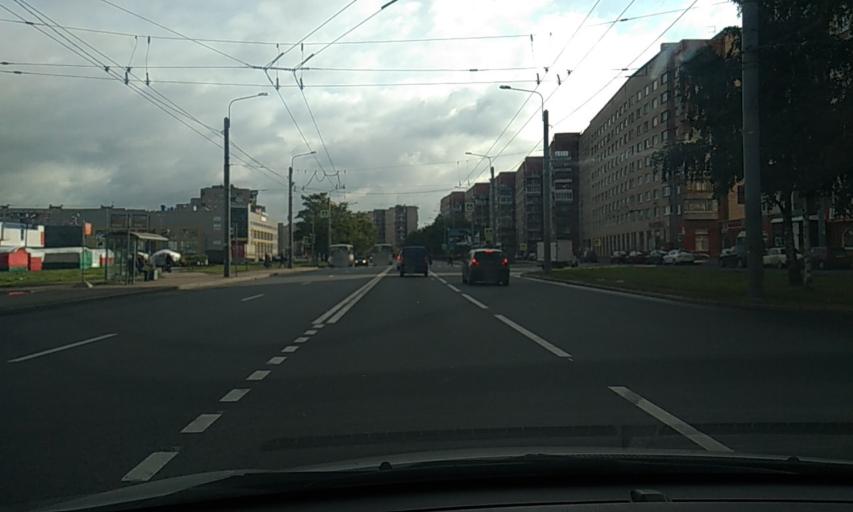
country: RU
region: St.-Petersburg
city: Uritsk
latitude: 59.8333
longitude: 30.2114
